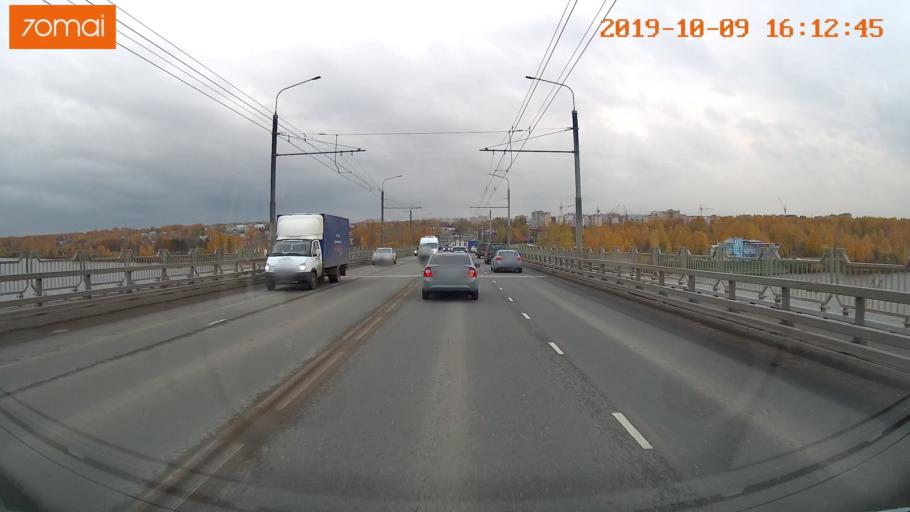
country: RU
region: Kostroma
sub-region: Kostromskoy Rayon
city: Kostroma
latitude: 57.7506
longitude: 40.9357
